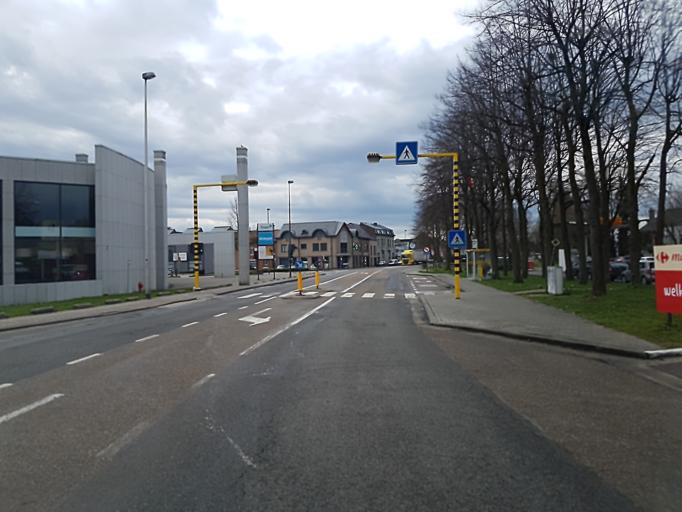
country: BE
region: Flanders
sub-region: Provincie Limburg
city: Tongeren
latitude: 50.7761
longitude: 5.4614
